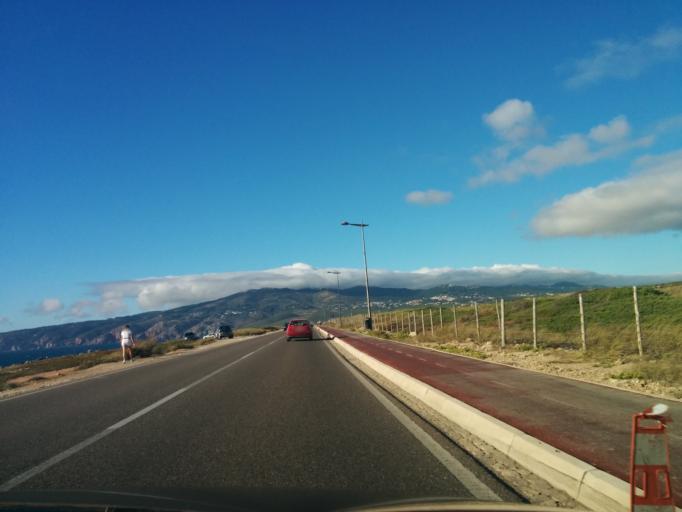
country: PT
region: Lisbon
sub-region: Cascais
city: Cascais
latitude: 38.7124
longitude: -9.4843
